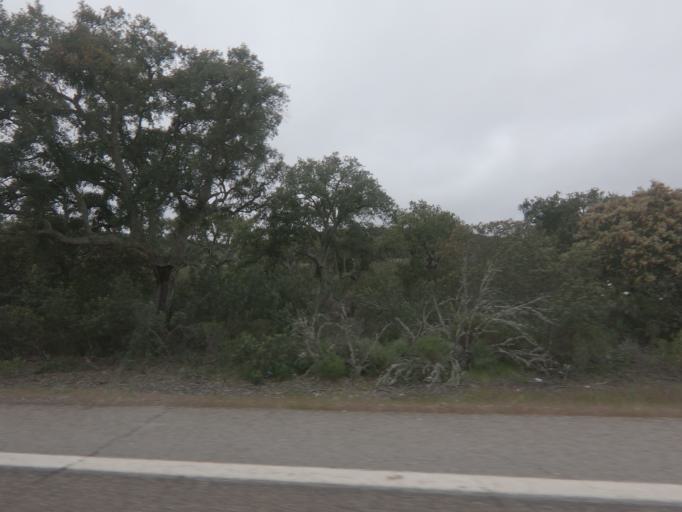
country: ES
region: Extremadura
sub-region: Provincia de Badajoz
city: Puebla de Obando
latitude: 39.2795
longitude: -6.5210
